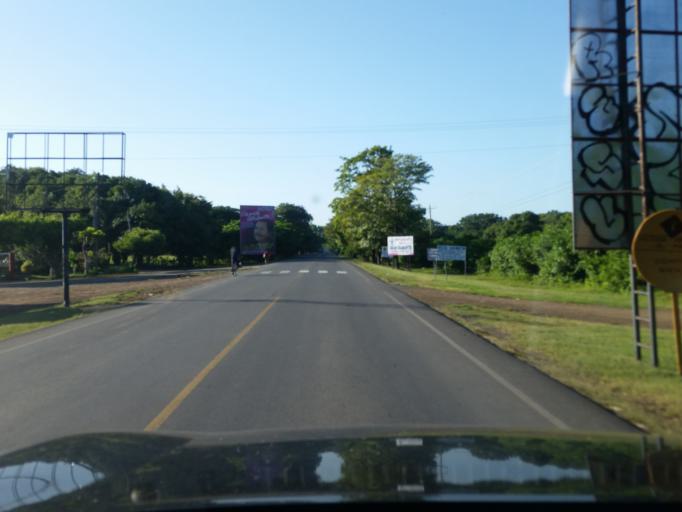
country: NI
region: Rivas
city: Rivas
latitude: 11.4299
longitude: -85.8103
